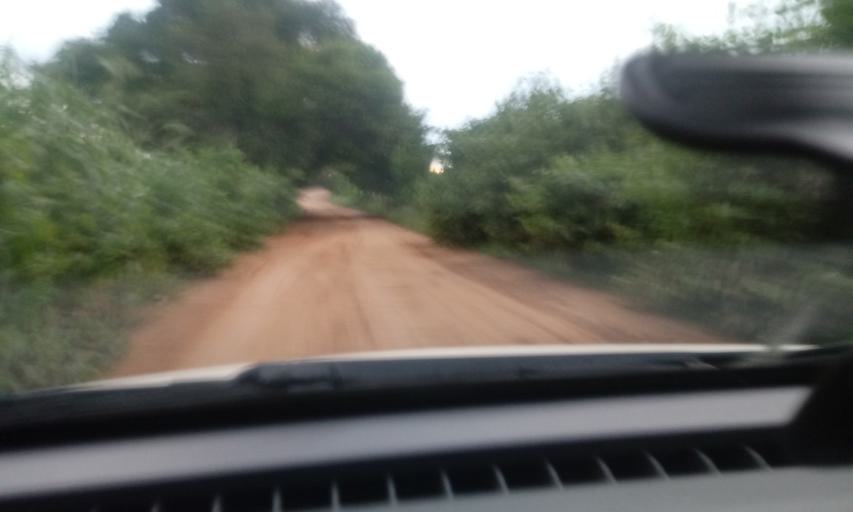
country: BR
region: Bahia
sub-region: Riacho De Santana
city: Riacho de Santana
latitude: -13.7979
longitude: -42.7348
